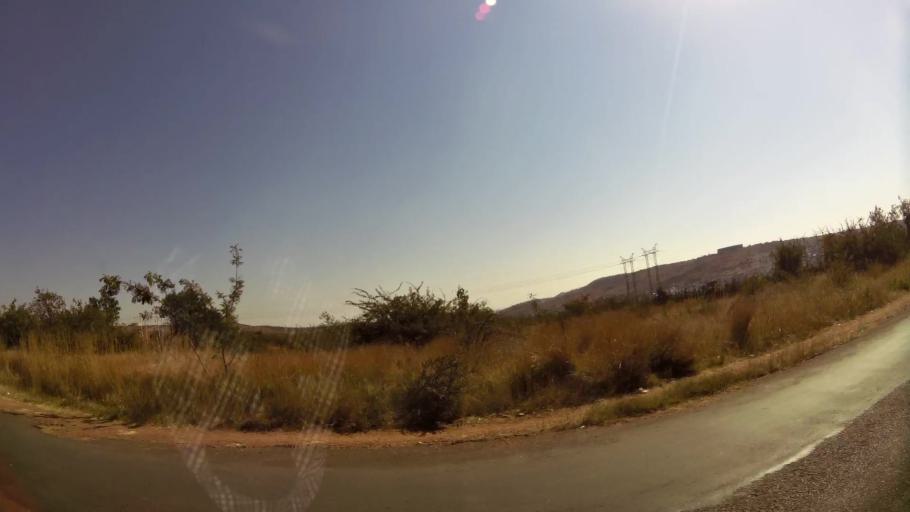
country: ZA
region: Gauteng
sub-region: City of Tshwane Metropolitan Municipality
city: Mabopane
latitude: -25.5391
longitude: 28.0815
